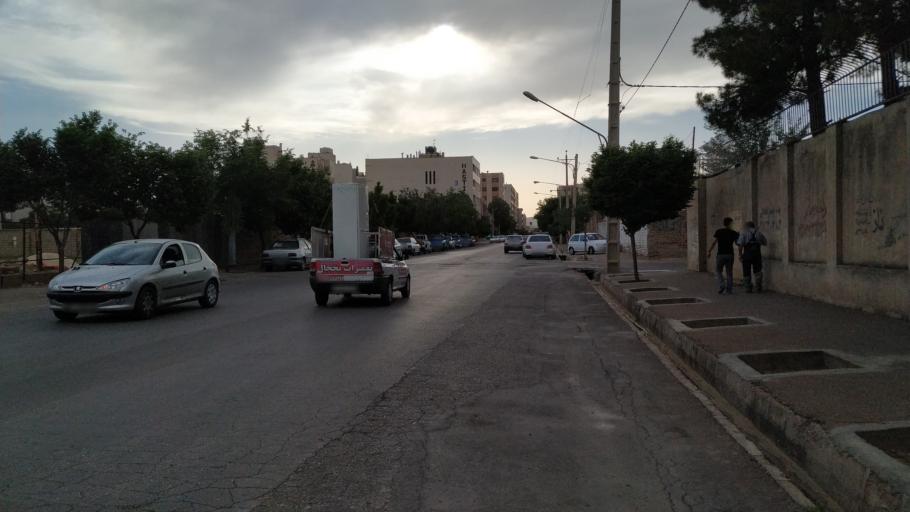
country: IR
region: Fars
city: Shiraz
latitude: 29.6091
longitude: 52.4867
